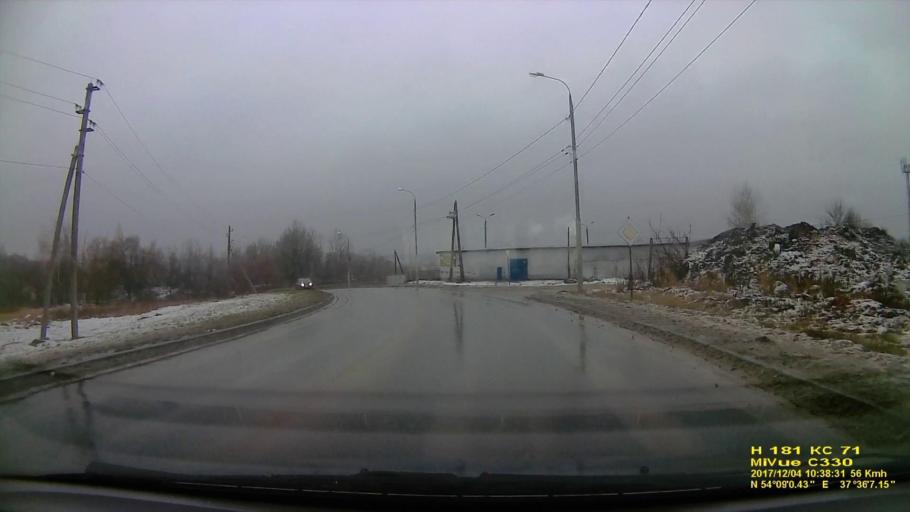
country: RU
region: Tula
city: Mendeleyevskiy
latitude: 54.1503
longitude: 37.6021
